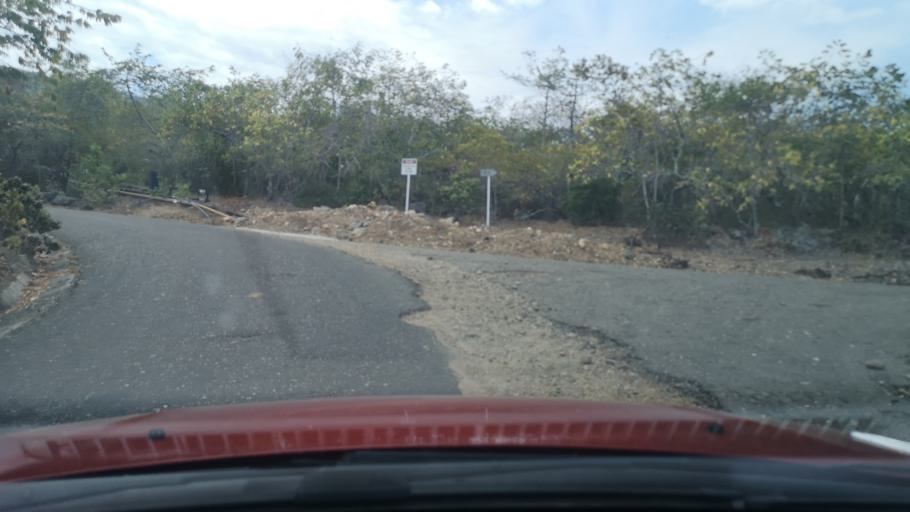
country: CO
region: Huila
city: Neiva
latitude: 2.9572
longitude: -75.3450
